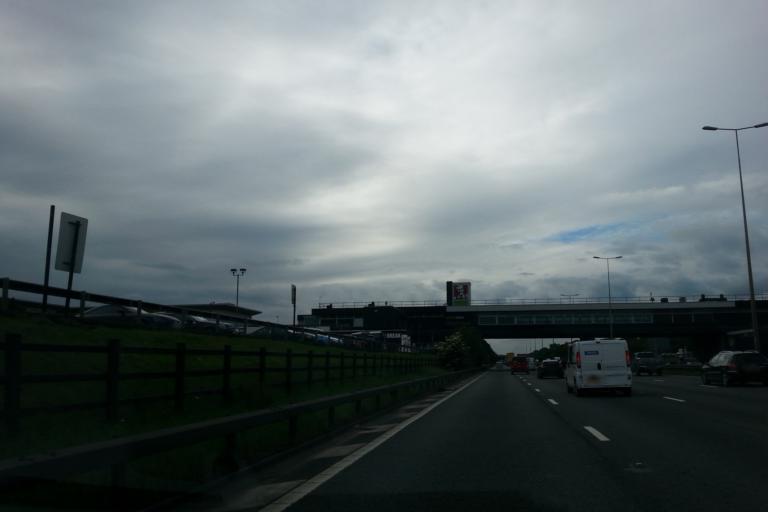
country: GB
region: England
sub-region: Leicestershire
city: Kirby Muxloe
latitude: 52.6181
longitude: -1.2050
